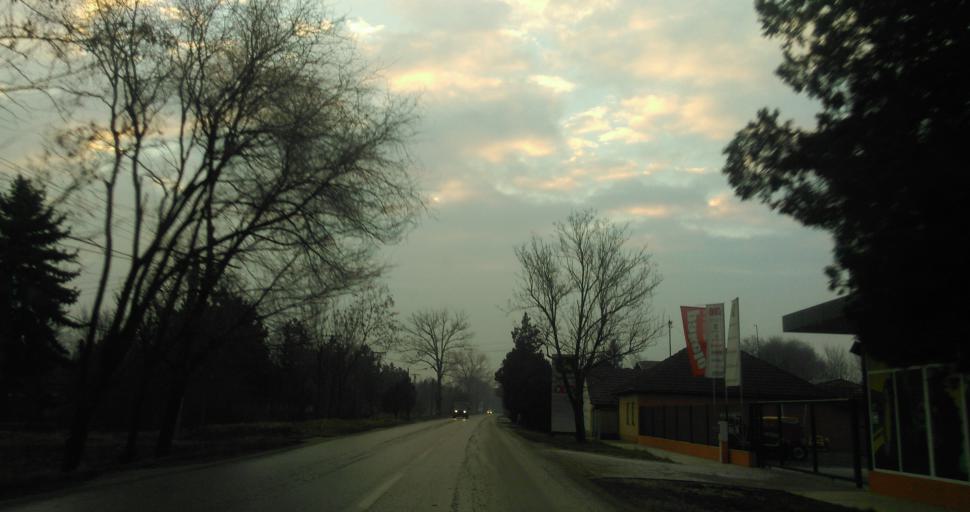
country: RS
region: Autonomna Pokrajina Vojvodina
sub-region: Juznobacki Okrug
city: Becej
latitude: 45.6320
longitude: 20.0328
